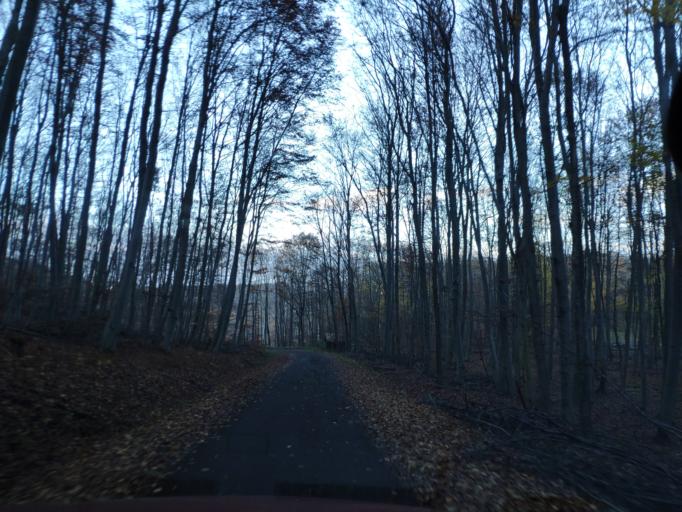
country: SK
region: Kosicky
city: Secovce
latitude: 48.5947
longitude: 21.5111
